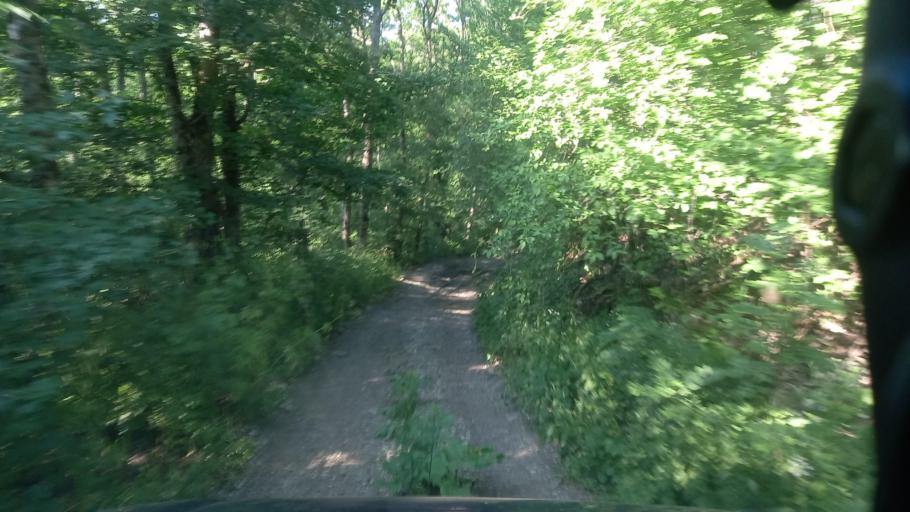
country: RU
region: Krasnodarskiy
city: Divnomorskoye
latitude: 44.5937
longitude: 38.2796
